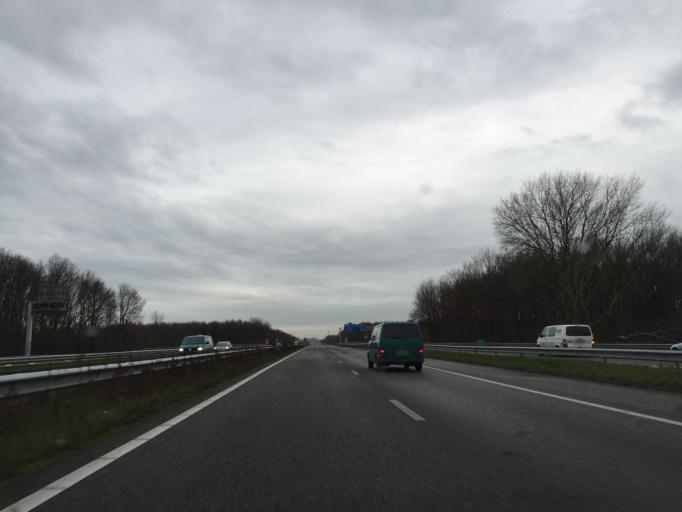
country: NL
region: North Brabant
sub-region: Roosendaal
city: Roosendaal
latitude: 51.5315
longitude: 4.4322
